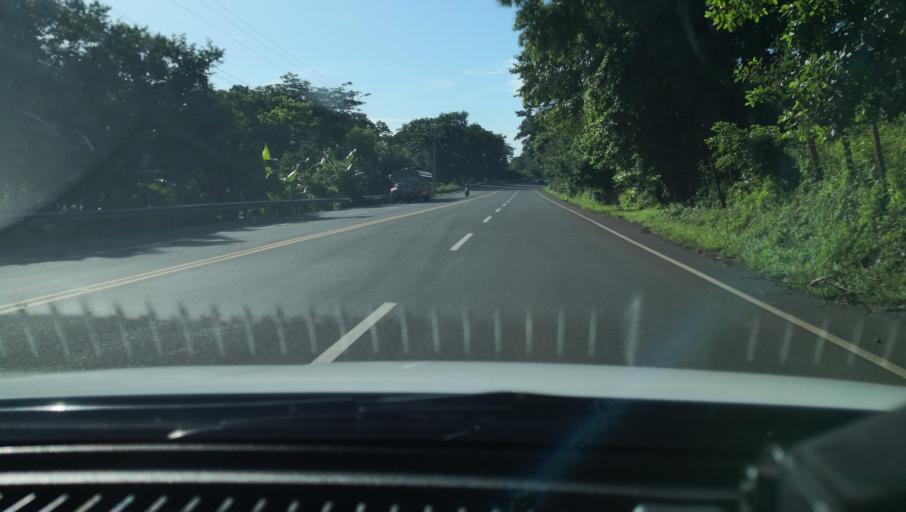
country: NI
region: Granada
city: Nandaime
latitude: 11.7885
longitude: -86.0611
